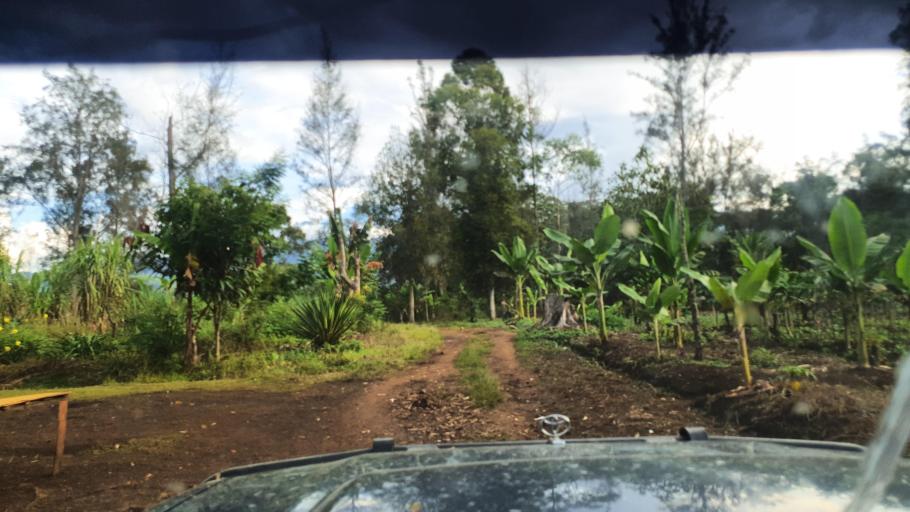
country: PG
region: Jiwaka
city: Minj
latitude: -5.9391
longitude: 144.8193
